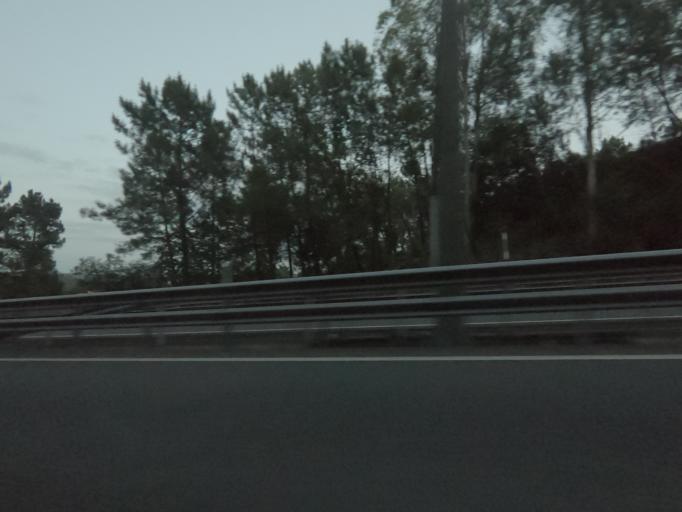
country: ES
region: Galicia
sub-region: Provincia de Pontevedra
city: Tui
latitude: 42.0654
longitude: -8.6474
